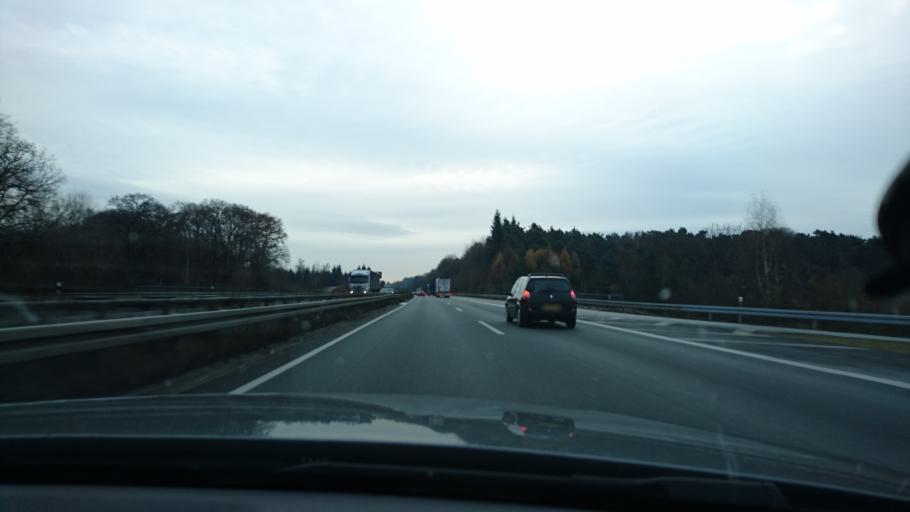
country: DE
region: North Rhine-Westphalia
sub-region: Regierungsbezirk Munster
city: Birgte
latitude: 52.2702
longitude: 7.6590
